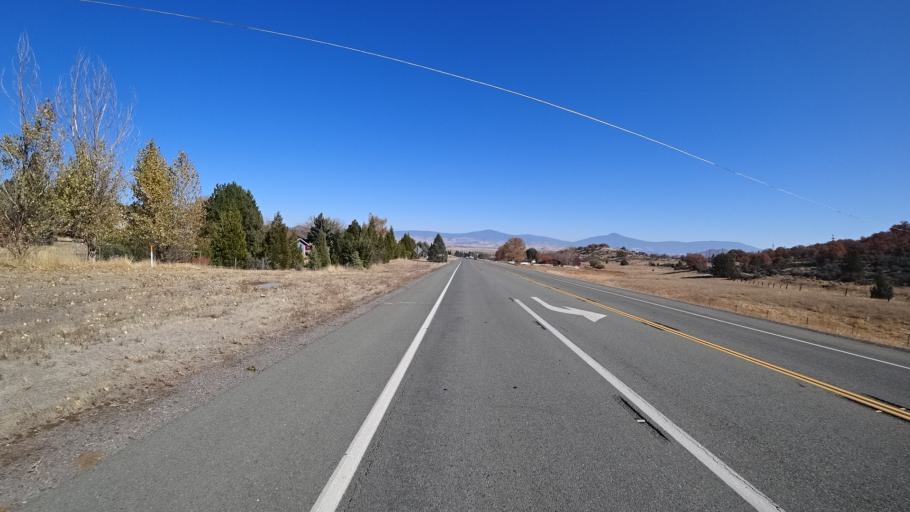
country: US
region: California
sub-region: Siskiyou County
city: Yreka
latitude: 41.7399
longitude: -122.6133
